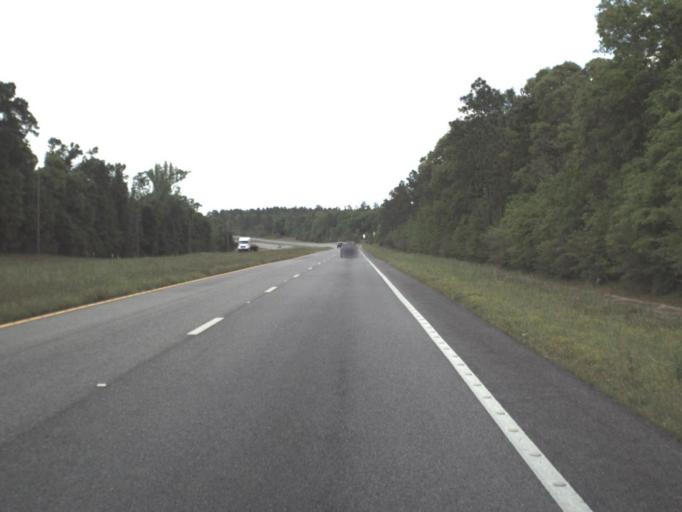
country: US
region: Florida
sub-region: Escambia County
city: Molino
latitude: 30.7574
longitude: -87.3436
